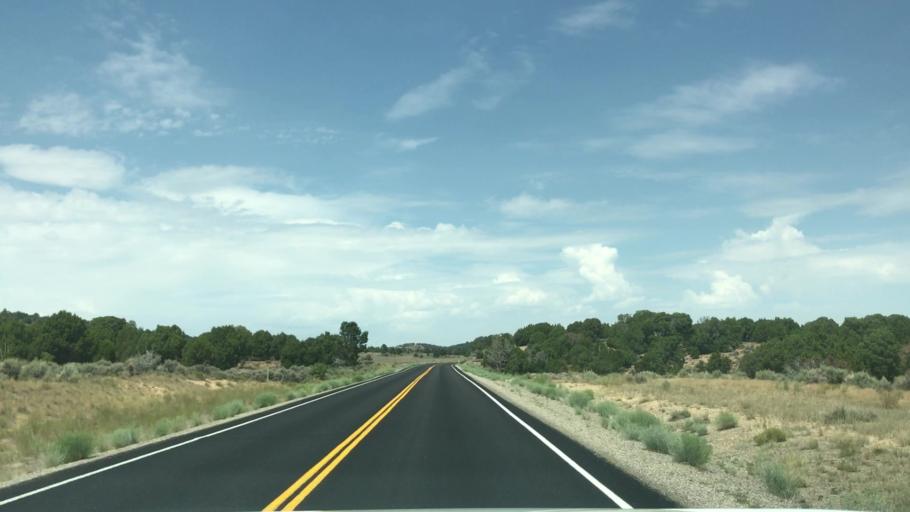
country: US
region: Nevada
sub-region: Eureka County
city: Eureka
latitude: 39.3912
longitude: -115.4545
